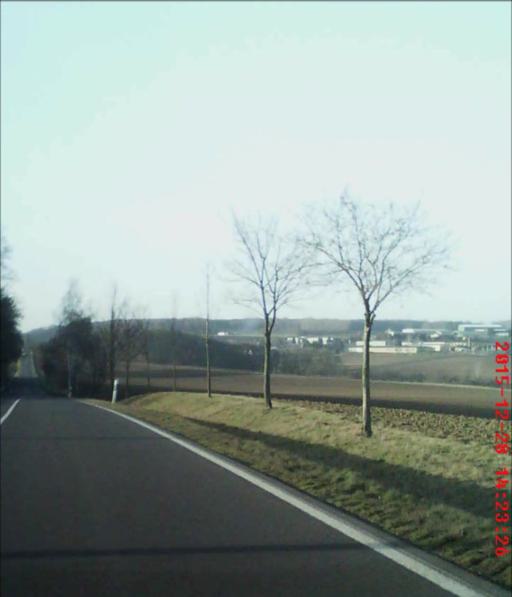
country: DE
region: Thuringia
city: Goldbach
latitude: 51.0546
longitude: 11.4605
